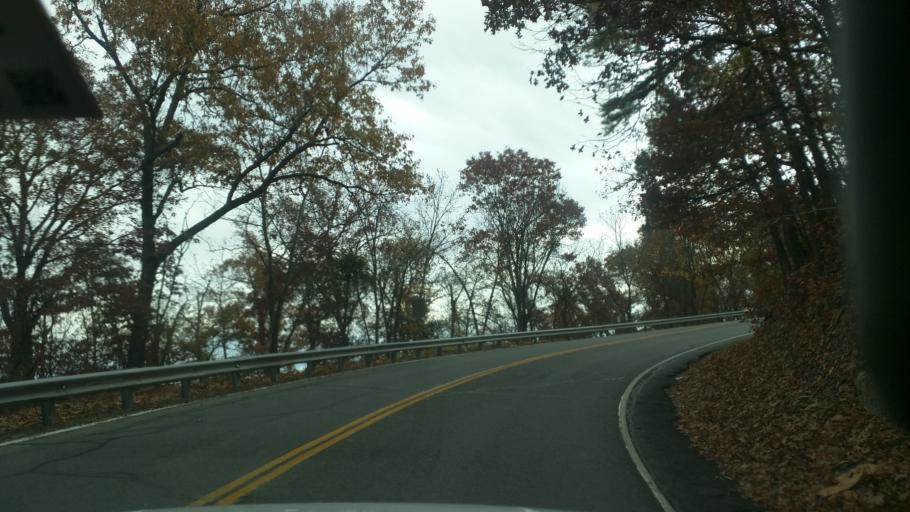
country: US
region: Oklahoma
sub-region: Cherokee County
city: Tahlequah
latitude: 35.9278
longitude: -94.8424
